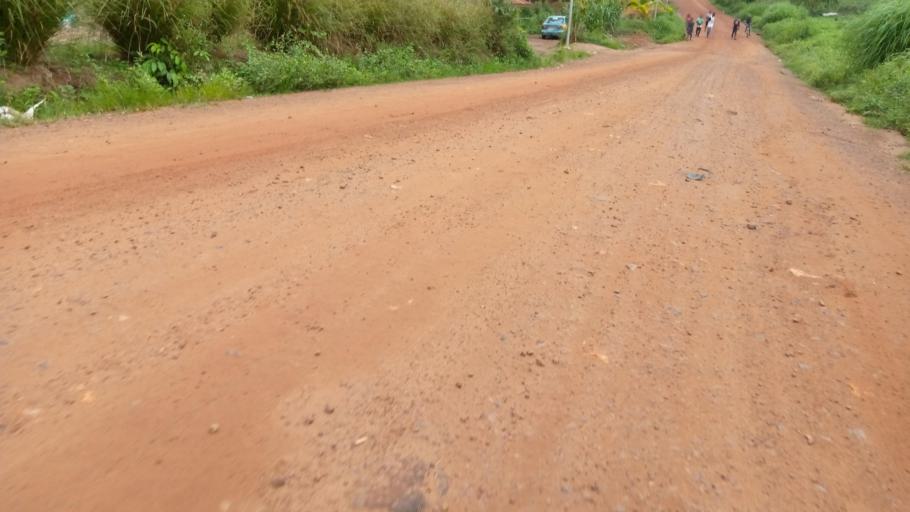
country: SL
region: Southern Province
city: Gandorhun
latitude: 7.4385
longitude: -11.8407
